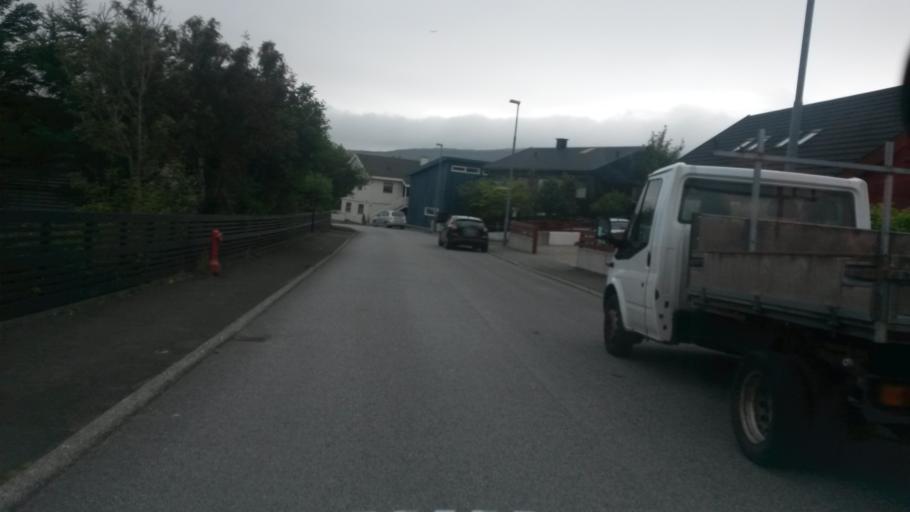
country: FO
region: Streymoy
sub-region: Torshavn
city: Torshavn
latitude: 62.0116
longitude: -6.7636
